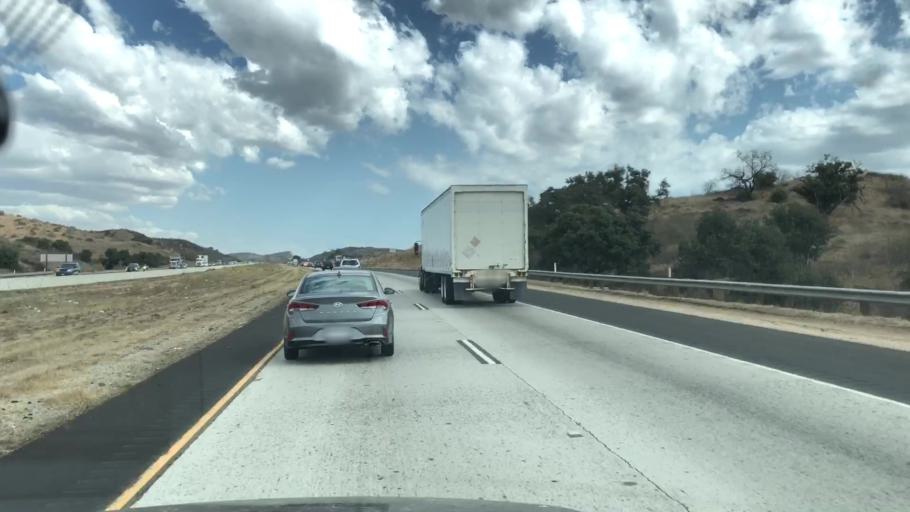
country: US
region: California
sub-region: Ventura County
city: Moorpark
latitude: 34.2923
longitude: -118.8321
